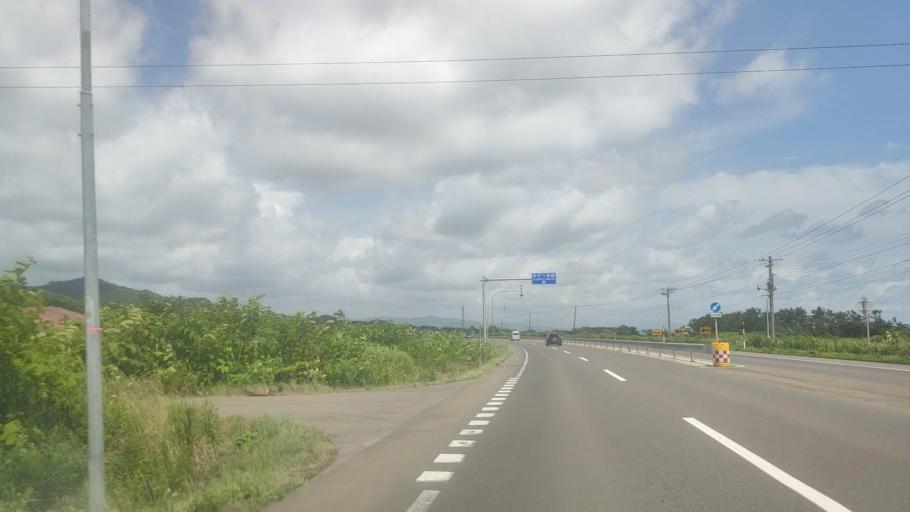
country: JP
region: Hokkaido
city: Niseko Town
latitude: 42.4485
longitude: 140.3303
